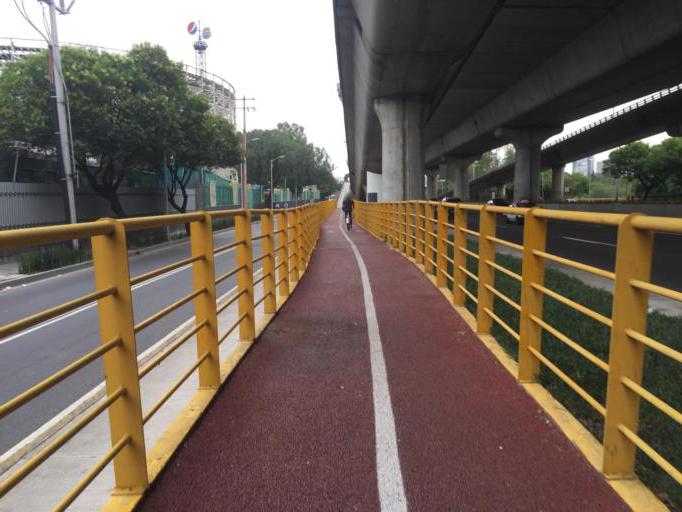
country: MX
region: Mexico City
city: Polanco
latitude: 19.4152
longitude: -99.1939
